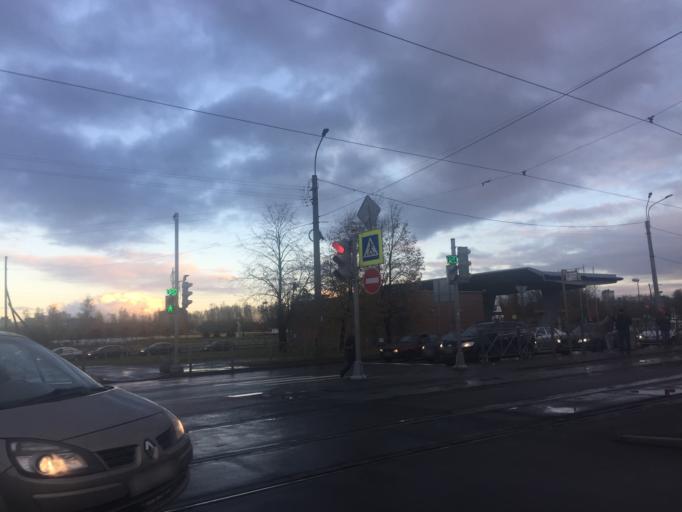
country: RU
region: St.-Petersburg
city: Obukhovo
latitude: 59.8896
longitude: 30.4637
